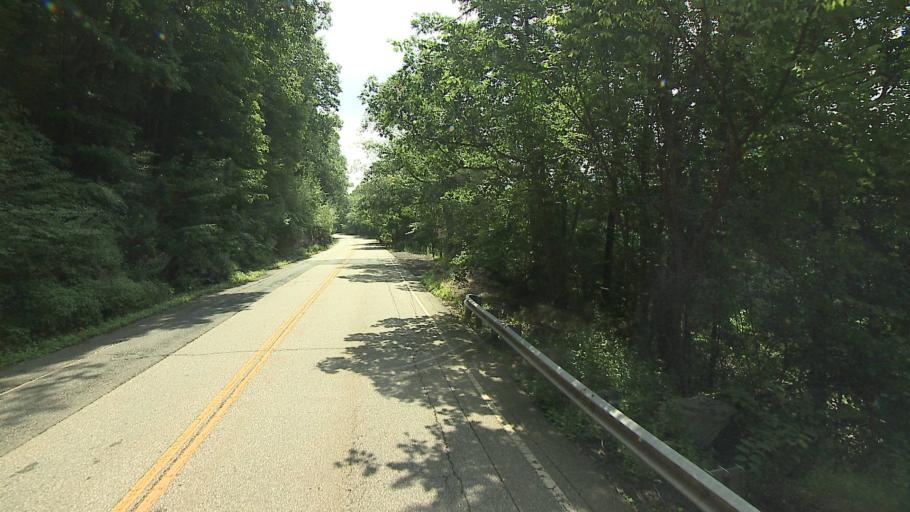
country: US
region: Connecticut
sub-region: Litchfield County
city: Thomaston
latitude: 41.6514
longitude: -73.0764
